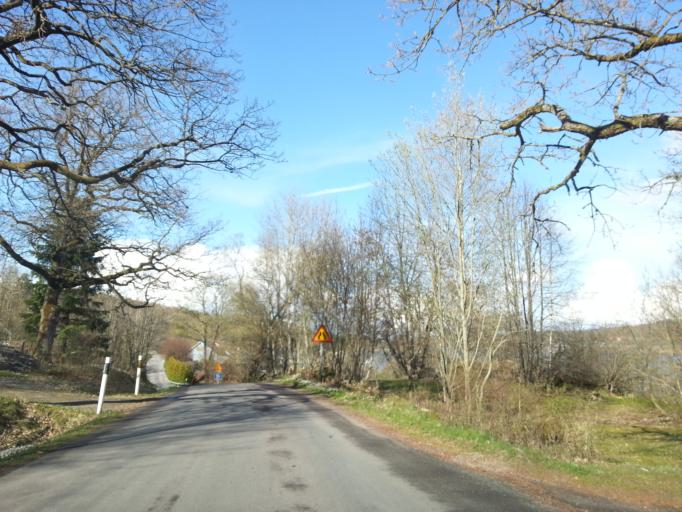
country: SE
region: Vaestra Goetaland
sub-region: Ale Kommun
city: Nodinge-Nol
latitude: 57.8990
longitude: 12.0359
